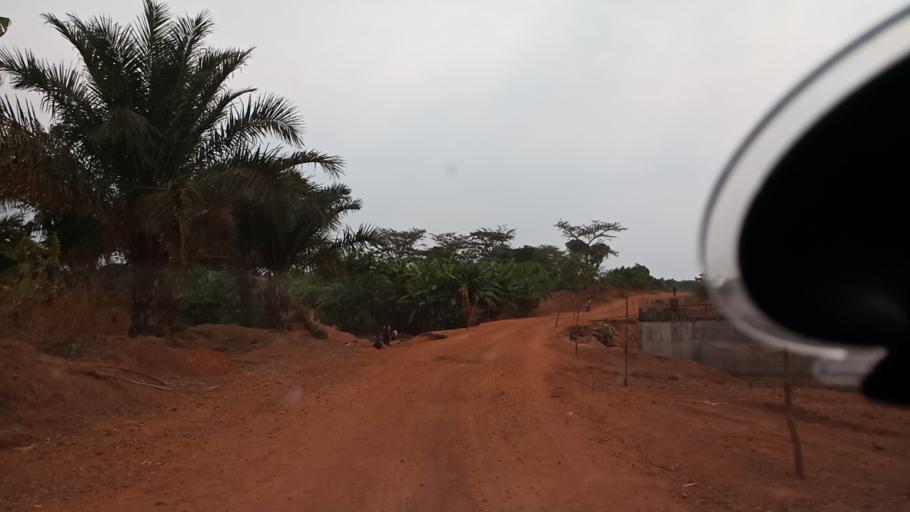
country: ZM
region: Luapula
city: Nchelenge
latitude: -9.0988
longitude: 28.3090
